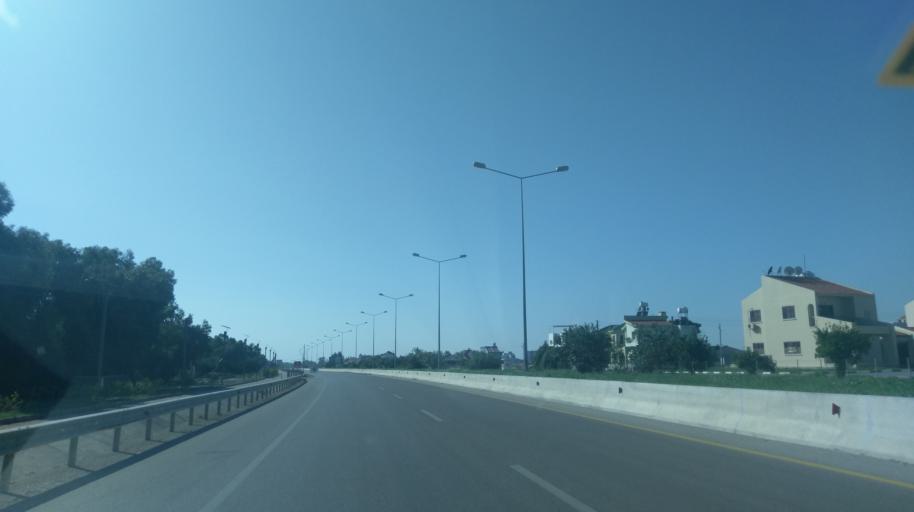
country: CY
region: Ammochostos
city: Trikomo
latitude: 35.2742
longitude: 33.9171
